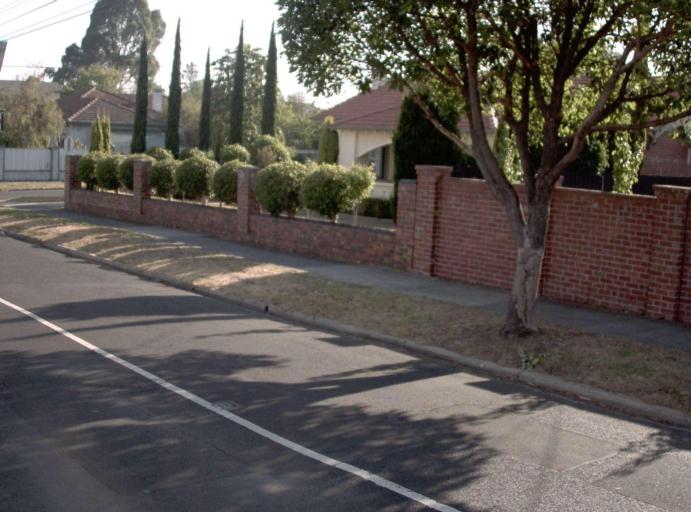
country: AU
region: Victoria
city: Murrumbeena
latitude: -37.9005
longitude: 145.0645
